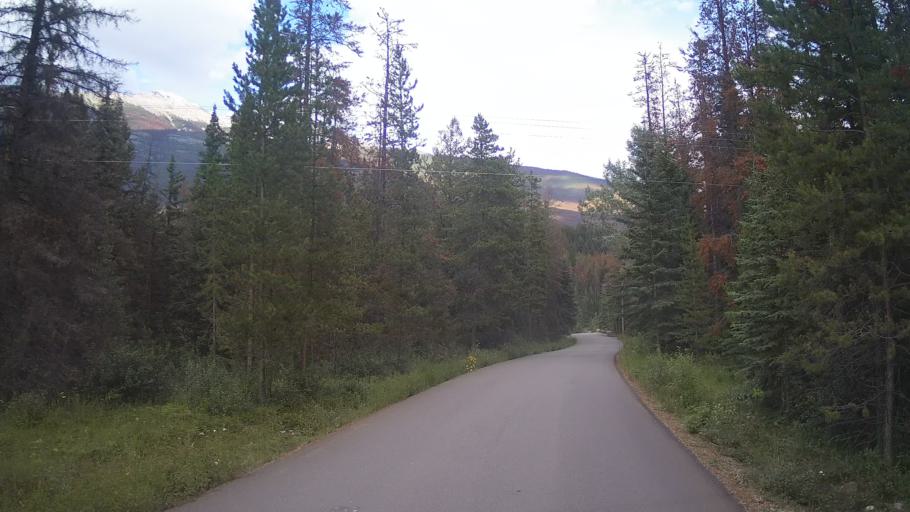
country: CA
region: Alberta
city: Jasper Park Lodge
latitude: 52.9204
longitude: -118.0202
